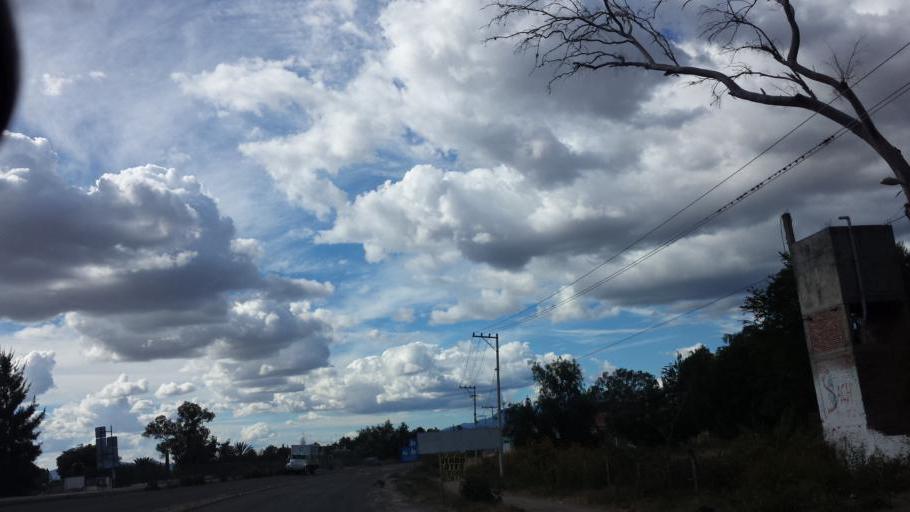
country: MX
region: Oaxaca
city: Tlacolula de Matamoros
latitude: 16.9518
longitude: -96.4671
